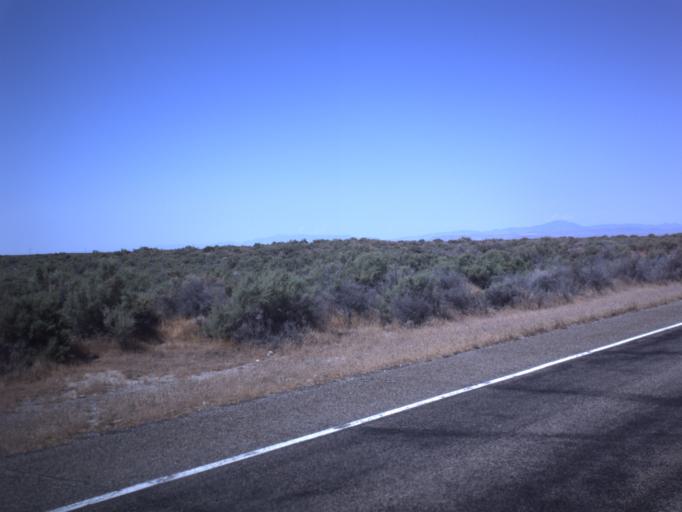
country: US
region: Utah
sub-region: Millard County
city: Delta
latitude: 39.4836
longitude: -112.5247
